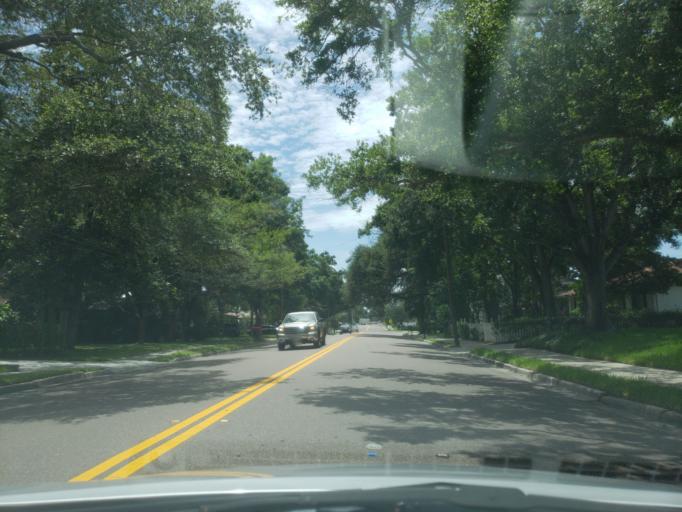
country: US
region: Florida
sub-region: Hillsborough County
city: Tampa
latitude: 27.9087
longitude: -82.4965
